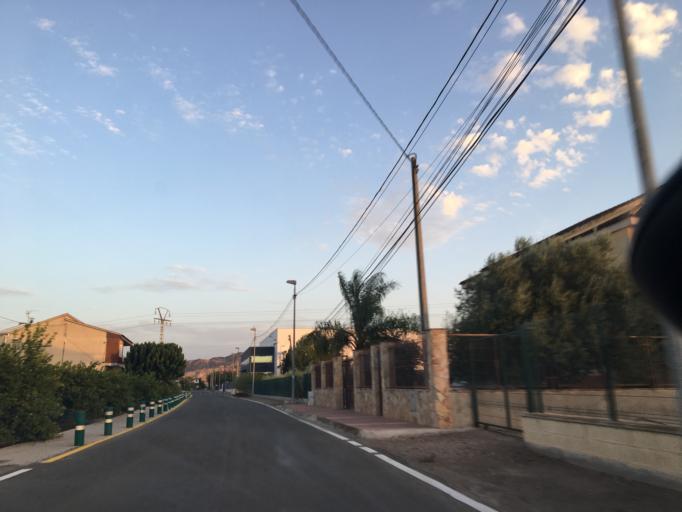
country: ES
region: Murcia
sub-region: Murcia
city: Santomera
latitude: 38.0210
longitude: -1.0535
